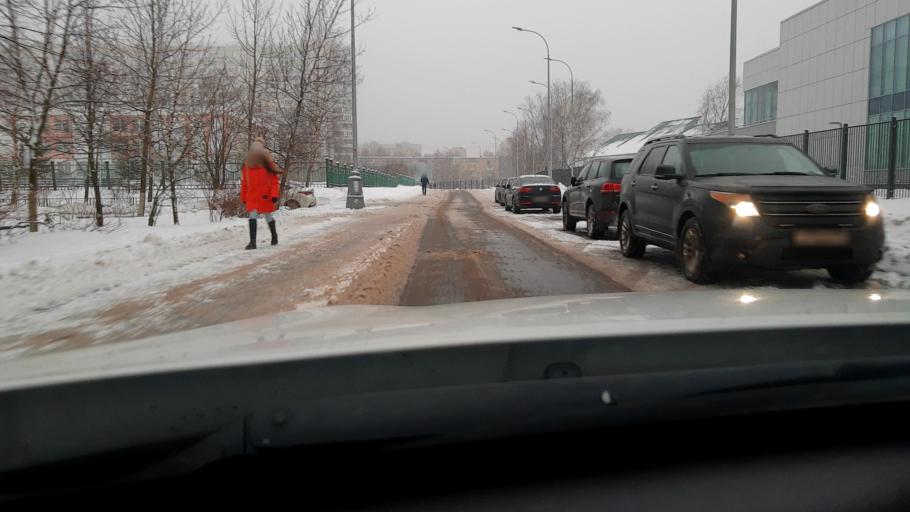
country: RU
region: Moscow
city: Severnyy
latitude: 55.9363
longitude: 37.5584
